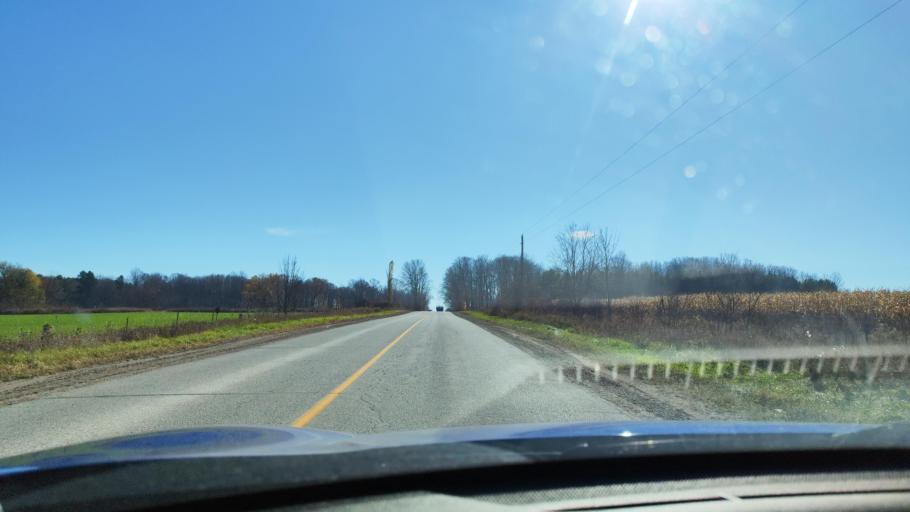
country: CA
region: Ontario
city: Wasaga Beach
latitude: 44.4586
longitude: -80.0030
